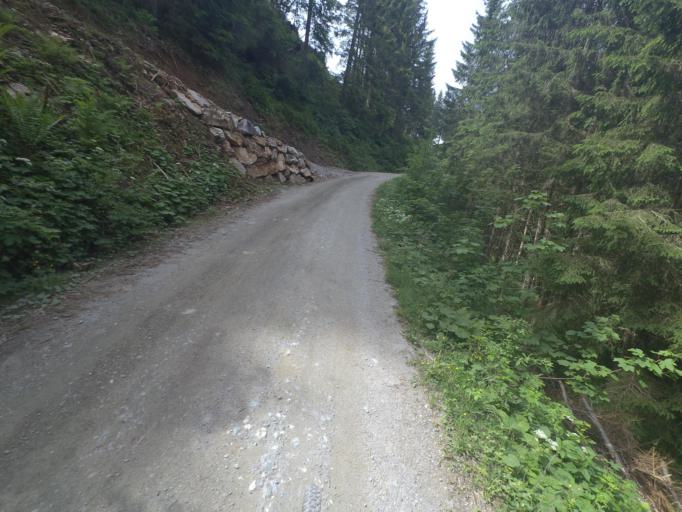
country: AT
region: Salzburg
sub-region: Politischer Bezirk Sankt Johann im Pongau
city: Muhlbach am Hochkonig
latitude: 47.3534
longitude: 13.1183
